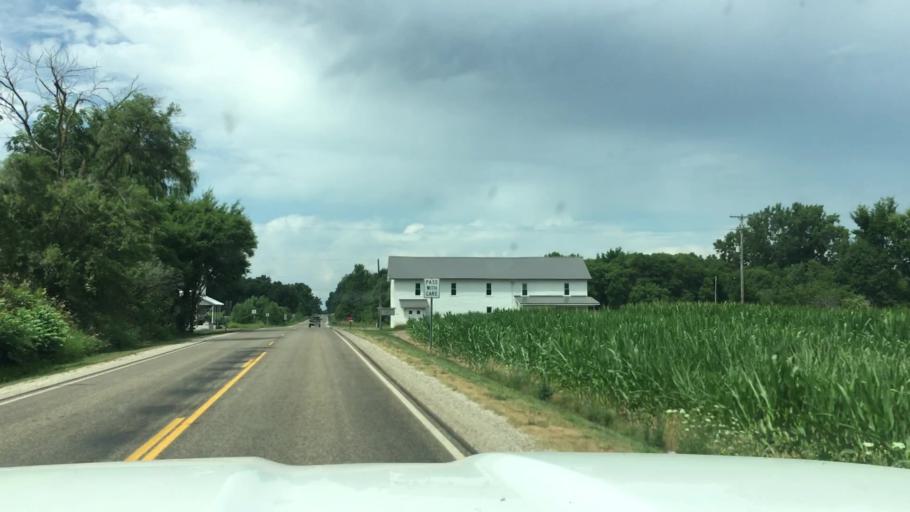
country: US
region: Michigan
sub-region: Montcalm County
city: Carson City
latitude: 43.2474
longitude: -84.7775
